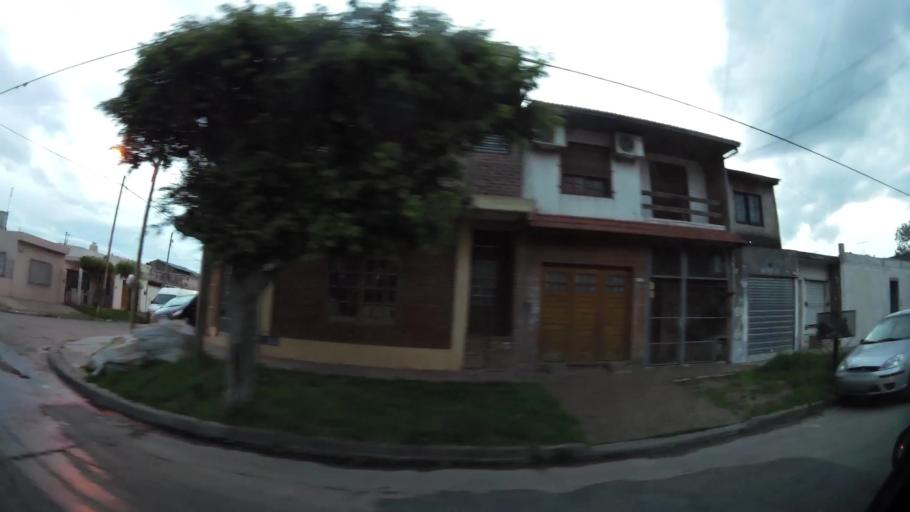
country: AR
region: Buenos Aires
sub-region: Partido de Quilmes
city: Quilmes
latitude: -34.7338
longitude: -58.2302
